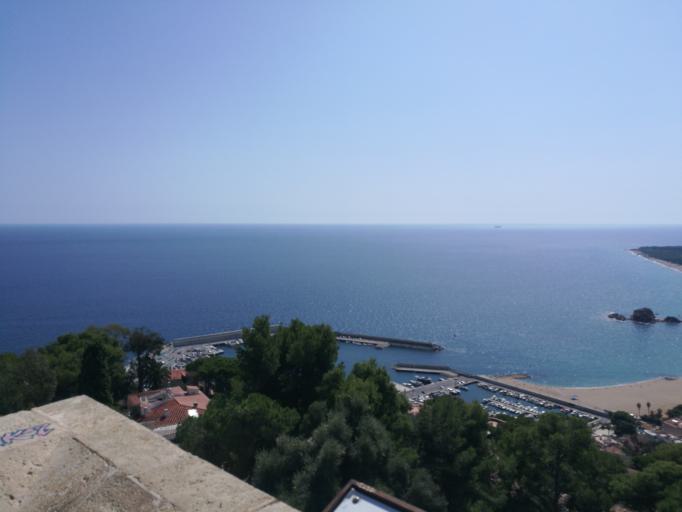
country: ES
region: Catalonia
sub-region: Provincia de Girona
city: Blanes
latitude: 41.6789
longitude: 2.7982
